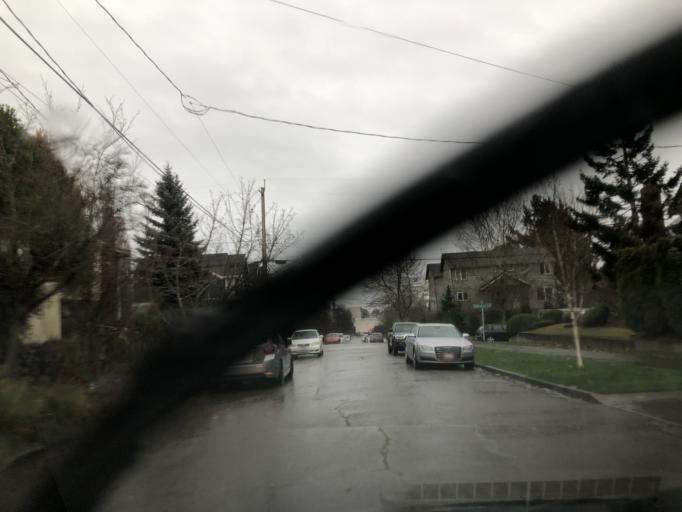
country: US
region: Washington
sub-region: King County
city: Seattle
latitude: 47.6602
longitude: -122.3528
